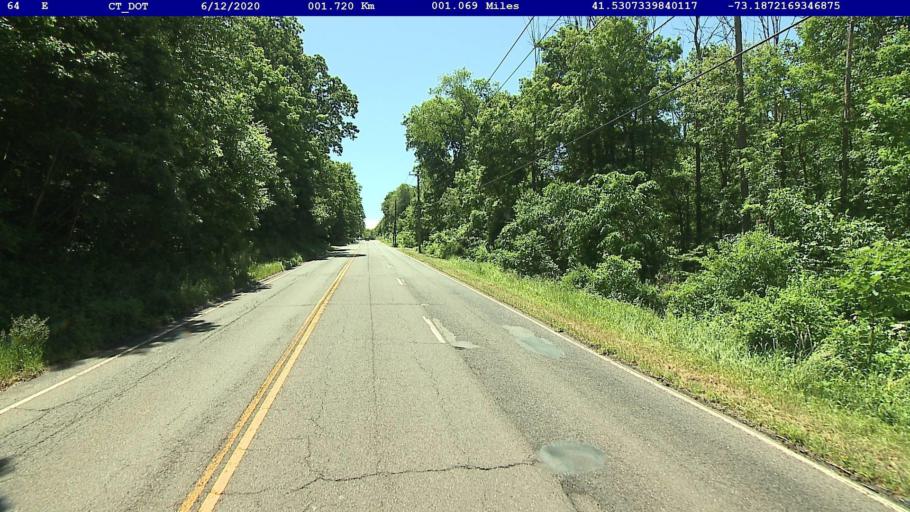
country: US
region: Connecticut
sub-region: Litchfield County
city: Woodbury Center
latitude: 41.5304
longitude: -73.1873
